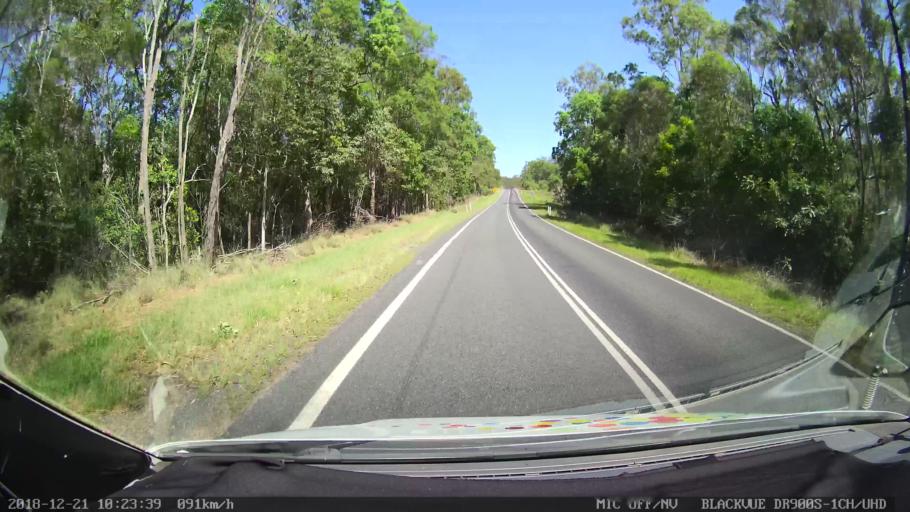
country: AU
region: New South Wales
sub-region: Clarence Valley
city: South Grafton
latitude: -29.6450
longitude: 152.7876
